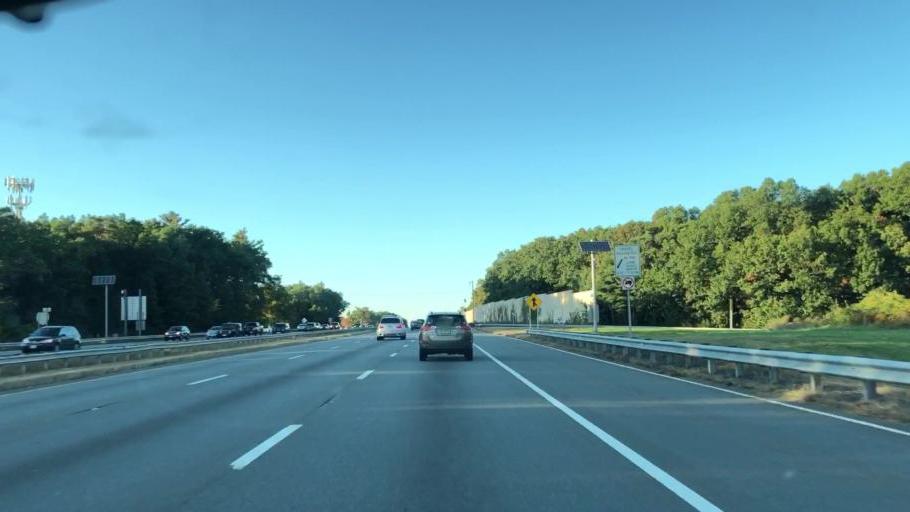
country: US
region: Massachusetts
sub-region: Essex County
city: Andover
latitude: 42.6228
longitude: -71.1771
